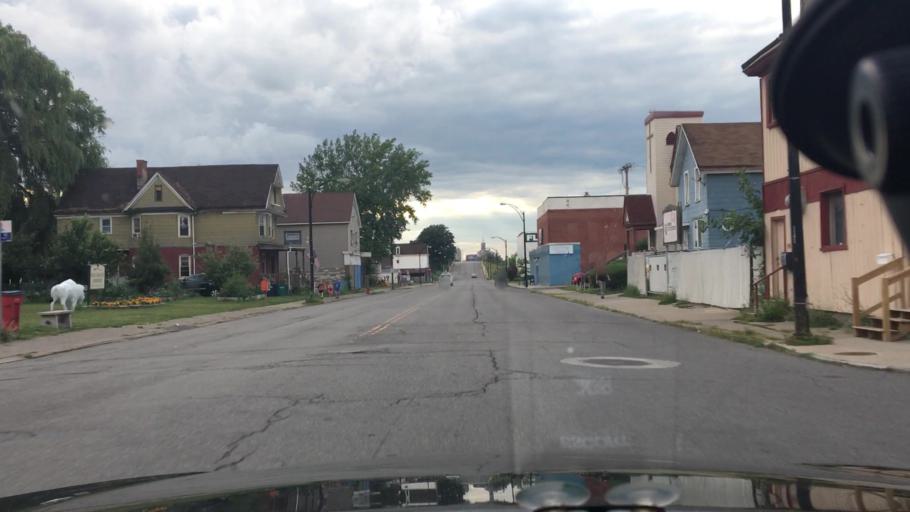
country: US
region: New York
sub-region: Erie County
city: West Seneca
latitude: 42.8706
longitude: -78.8344
